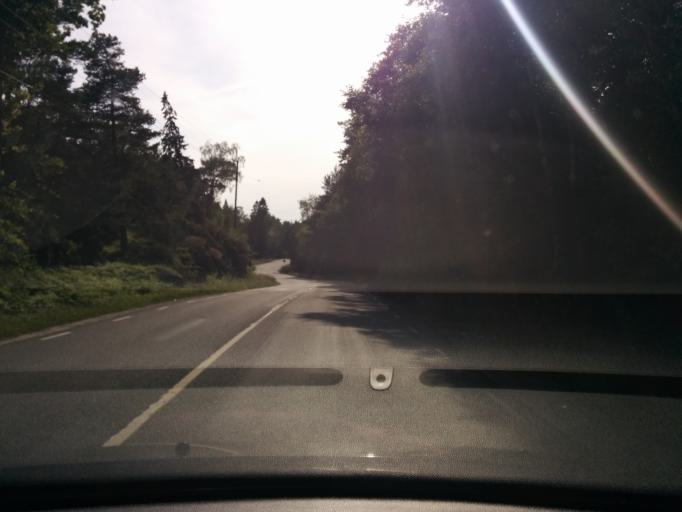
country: SE
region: Stockholm
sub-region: Varmdo Kommun
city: Holo
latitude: 59.3148
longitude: 18.7193
